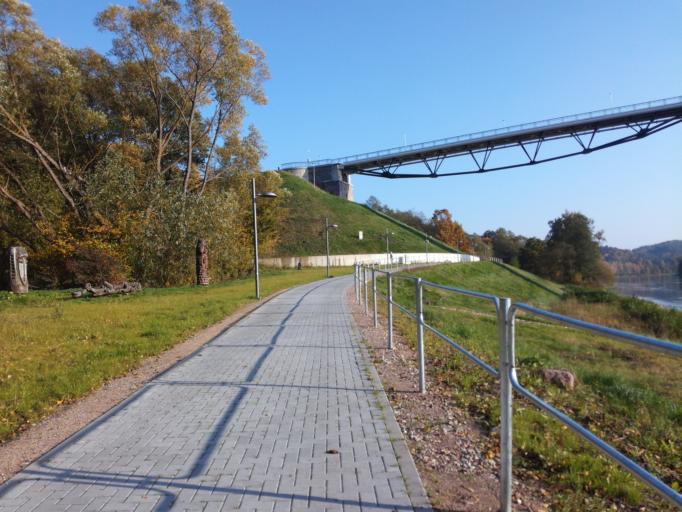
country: LT
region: Alytaus apskritis
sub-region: Alytus
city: Alytus
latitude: 54.3945
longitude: 24.0810
